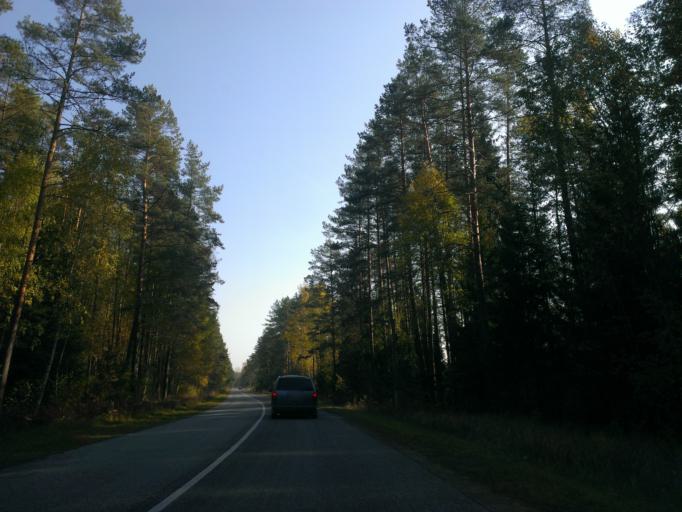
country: LV
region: Garkalne
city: Garkalne
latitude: 57.0155
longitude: 24.4444
